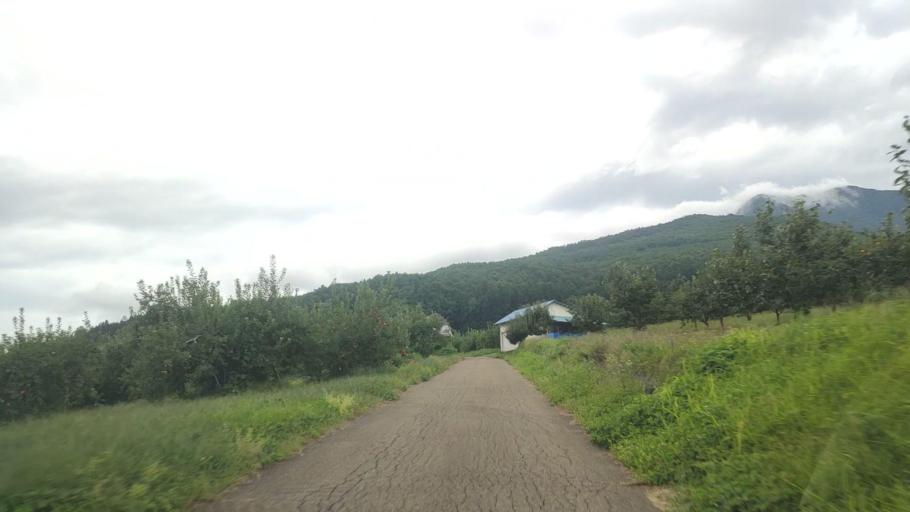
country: JP
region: Nagano
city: Nakano
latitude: 36.7771
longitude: 138.3860
